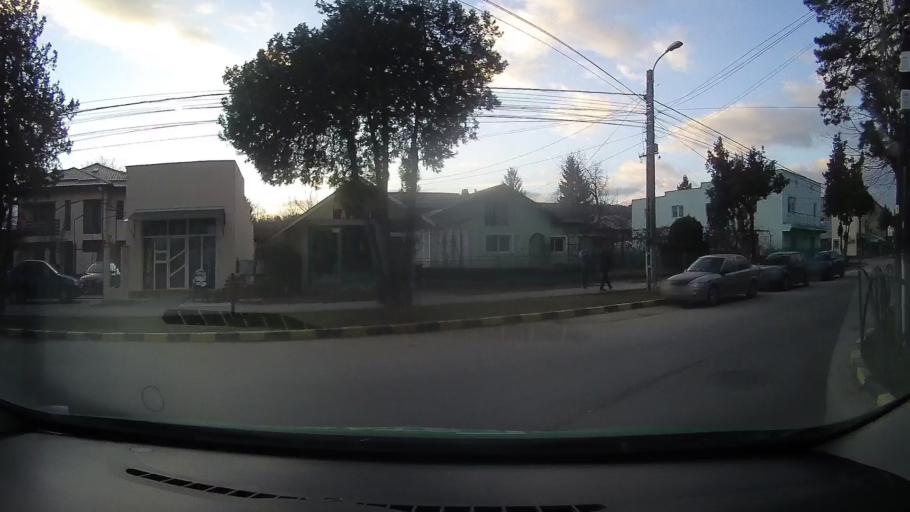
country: RO
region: Dambovita
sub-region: Municipiul Moreni
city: Moreni
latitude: 44.9821
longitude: 25.6395
